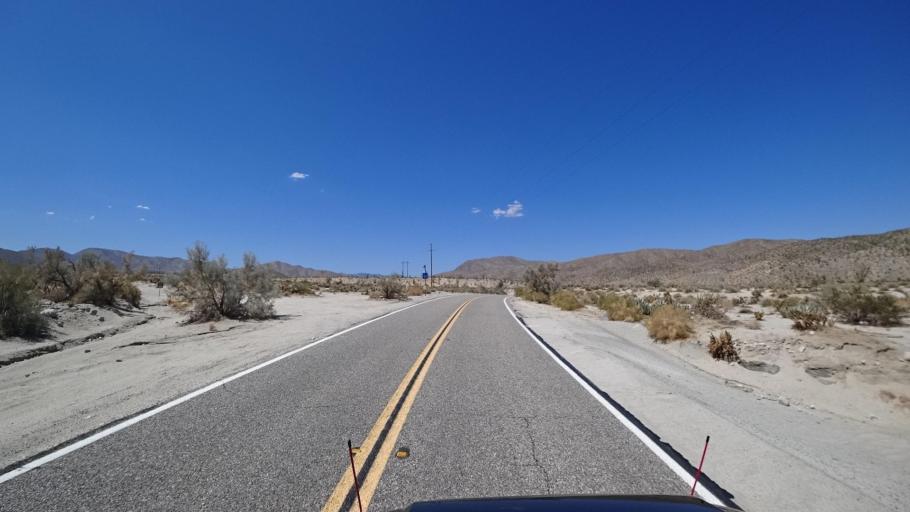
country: US
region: California
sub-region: San Diego County
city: Borrego Springs
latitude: 33.1321
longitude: -116.3112
